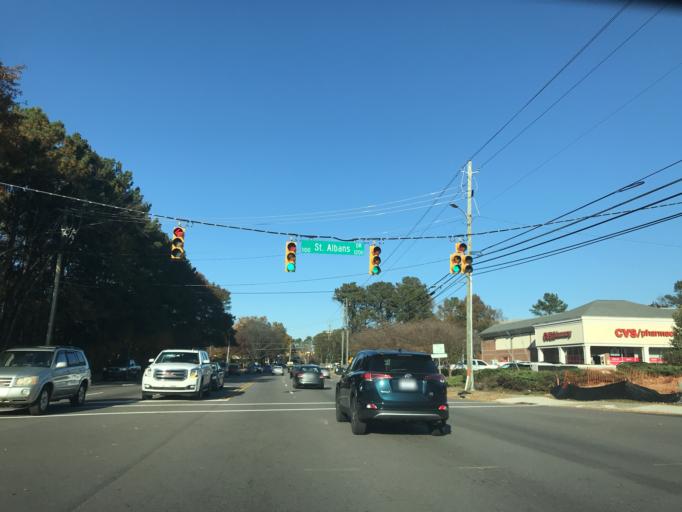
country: US
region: North Carolina
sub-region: Wake County
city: Raleigh
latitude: 35.8305
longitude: -78.6188
